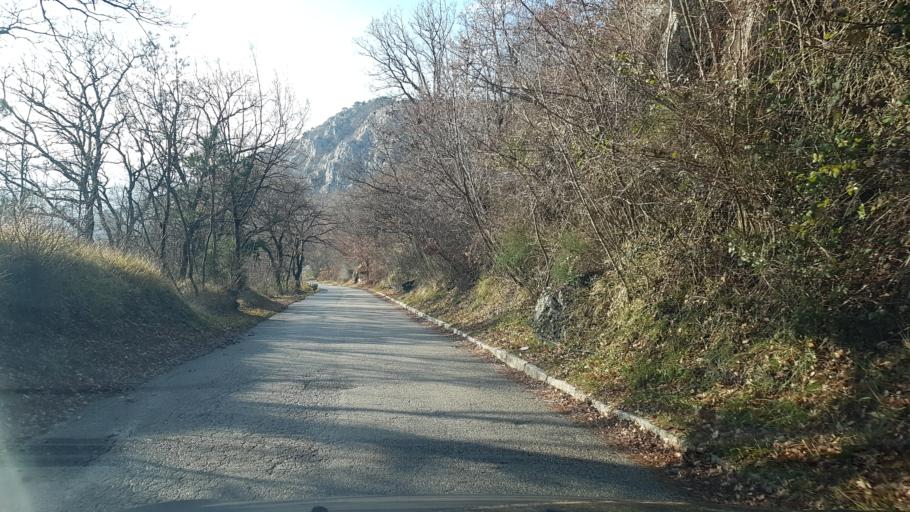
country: IT
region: Friuli Venezia Giulia
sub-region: Provincia di Trieste
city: Dolina
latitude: 45.6267
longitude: 13.8691
